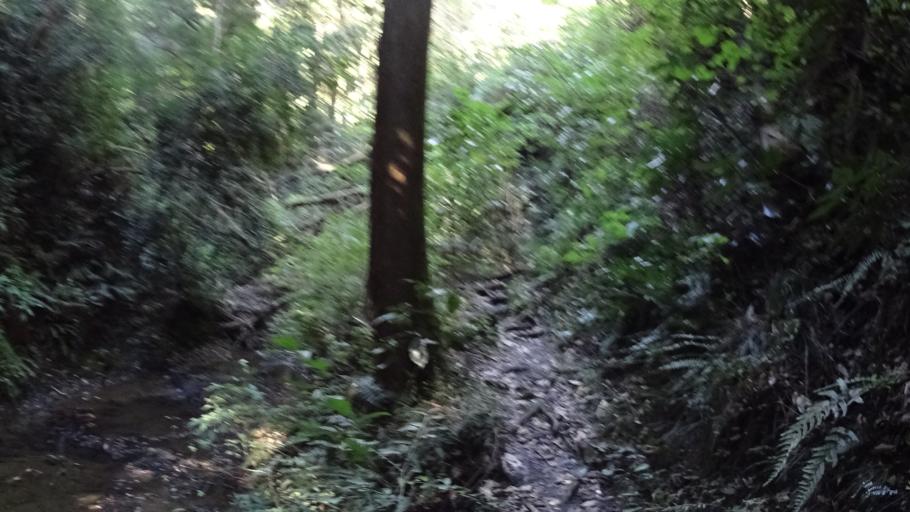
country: JP
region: Kanagawa
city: Hayama
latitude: 35.2803
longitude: 139.6081
